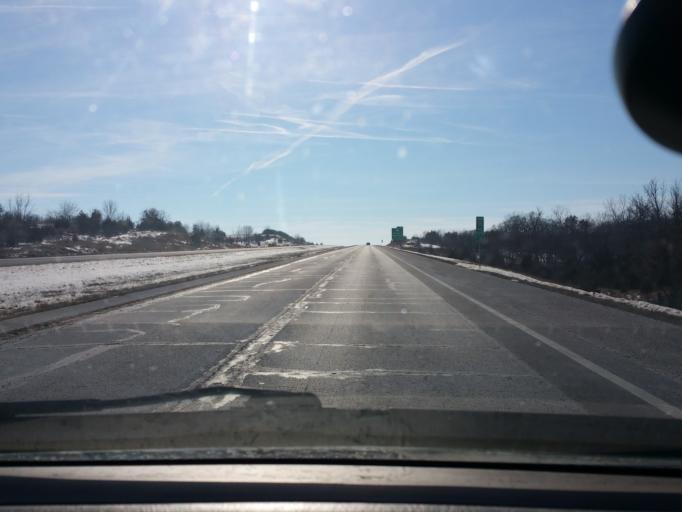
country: US
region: Missouri
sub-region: Harrison County
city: Bethany
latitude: 40.2307
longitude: -94.0131
